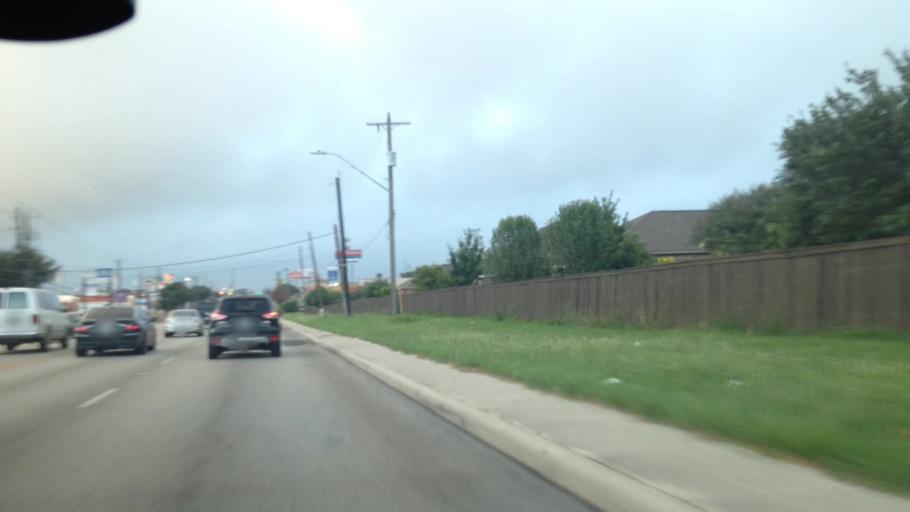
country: US
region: Texas
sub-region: Bexar County
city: Live Oak
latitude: 29.5718
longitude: -98.3806
